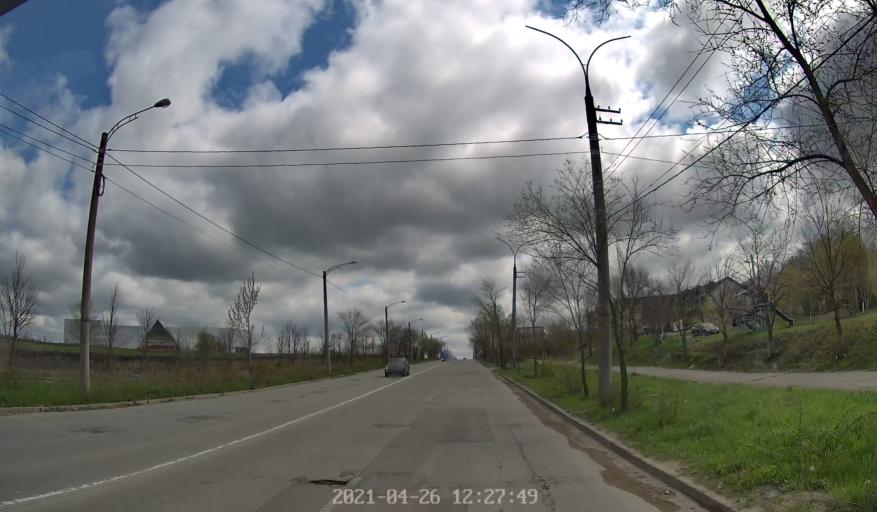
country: MD
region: Chisinau
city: Stauceni
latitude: 47.0682
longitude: 28.8831
